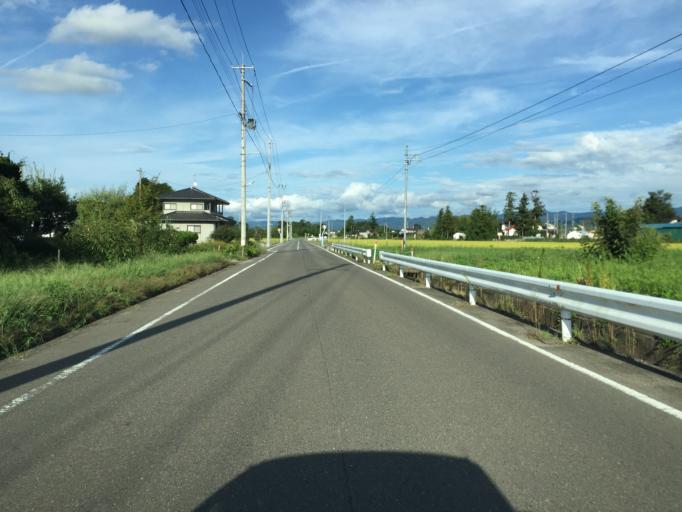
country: JP
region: Fukushima
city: Hobaramachi
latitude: 37.8135
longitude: 140.5341
